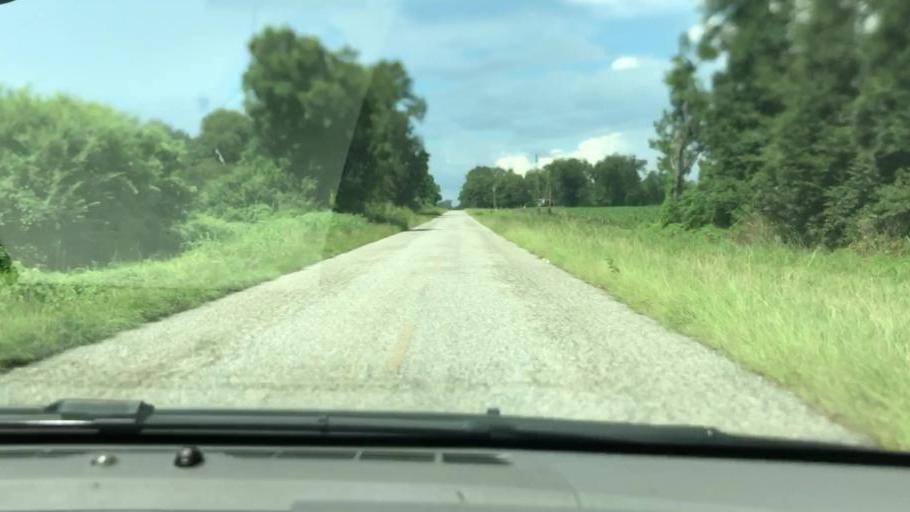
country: US
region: Georgia
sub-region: Early County
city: Blakely
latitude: 31.2045
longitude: -85.0036
